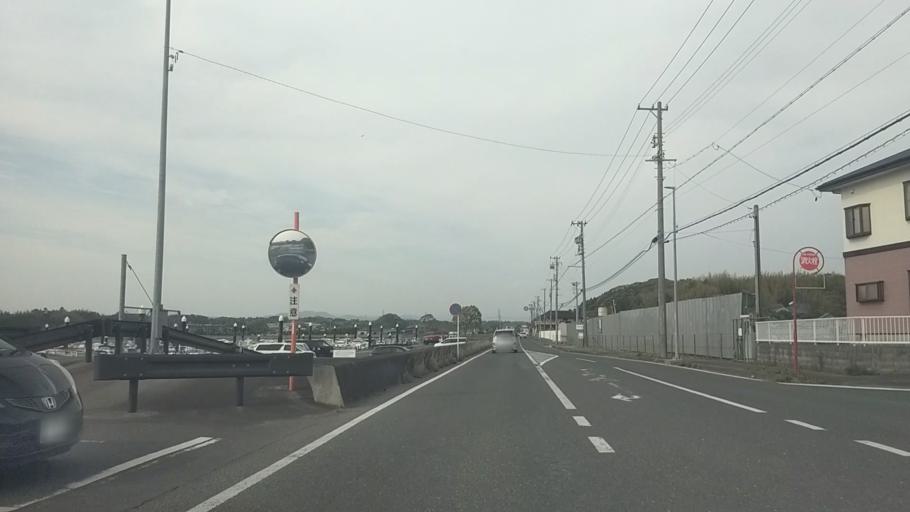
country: JP
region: Shizuoka
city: Hamamatsu
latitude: 34.7324
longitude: 137.6395
